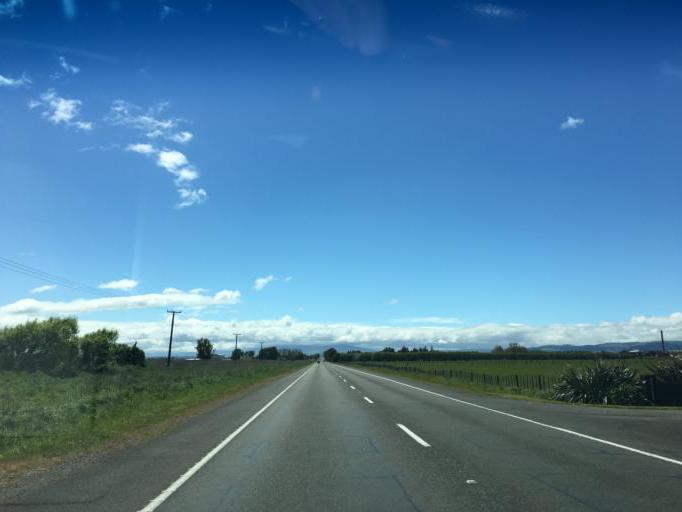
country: NZ
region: Manawatu-Wanganui
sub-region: Palmerston North City
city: Palmerston North
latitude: -40.3905
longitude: 175.5276
